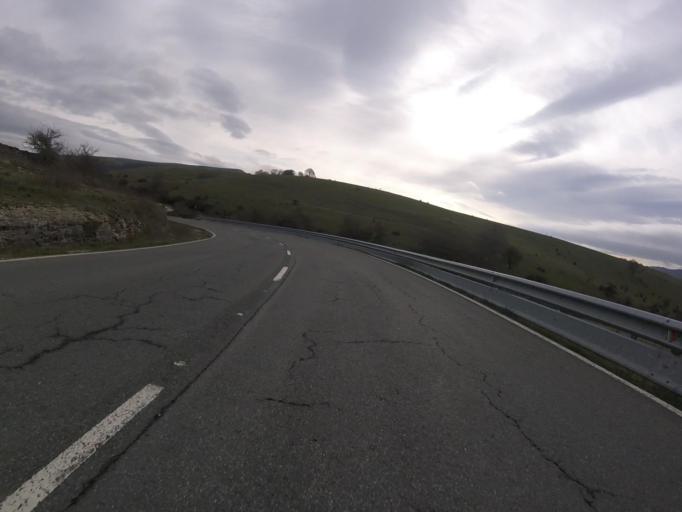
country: ES
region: Navarre
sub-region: Provincia de Navarra
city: Lezaun
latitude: 42.8444
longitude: -2.0141
